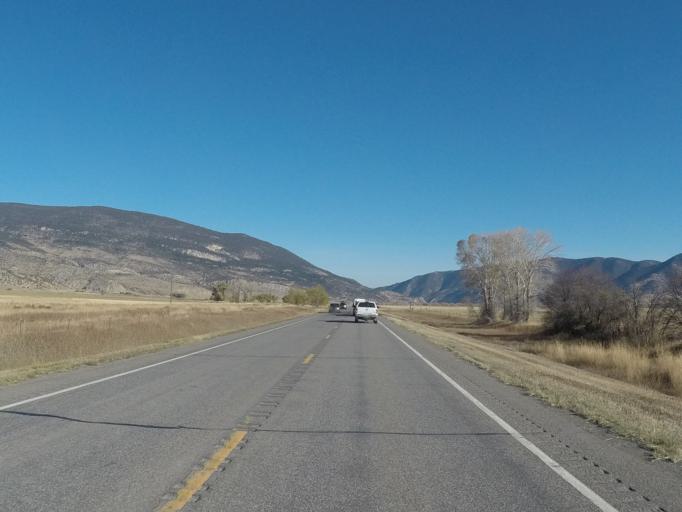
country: US
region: Montana
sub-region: Park County
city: Livingston
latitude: 45.5416
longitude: -110.6009
